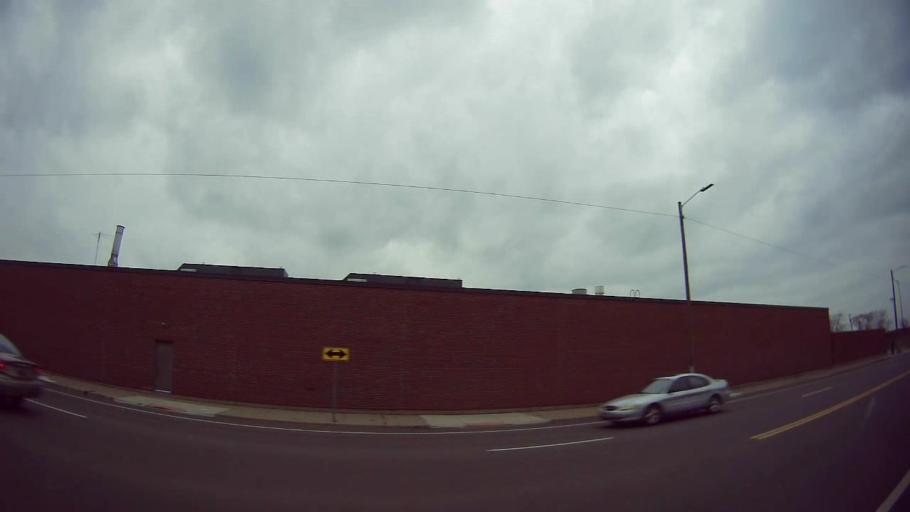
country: US
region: Michigan
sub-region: Wayne County
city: Grosse Pointe Park
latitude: 42.3868
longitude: -82.9851
